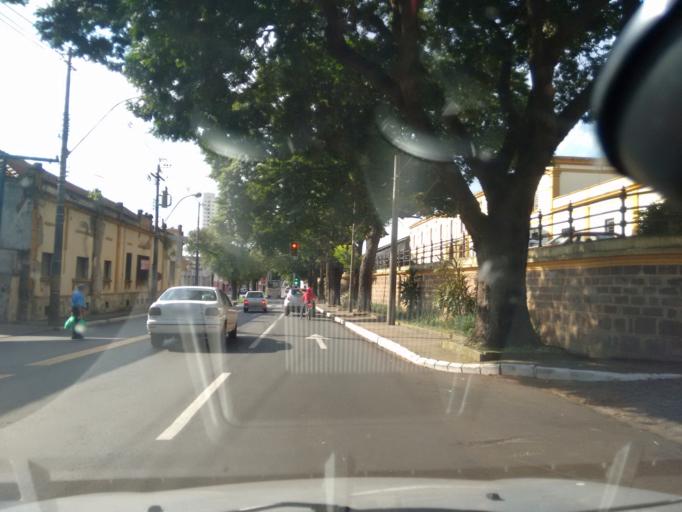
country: BR
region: Sao Paulo
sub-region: Araraquara
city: Araraquara
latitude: -21.7946
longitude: -48.1714
